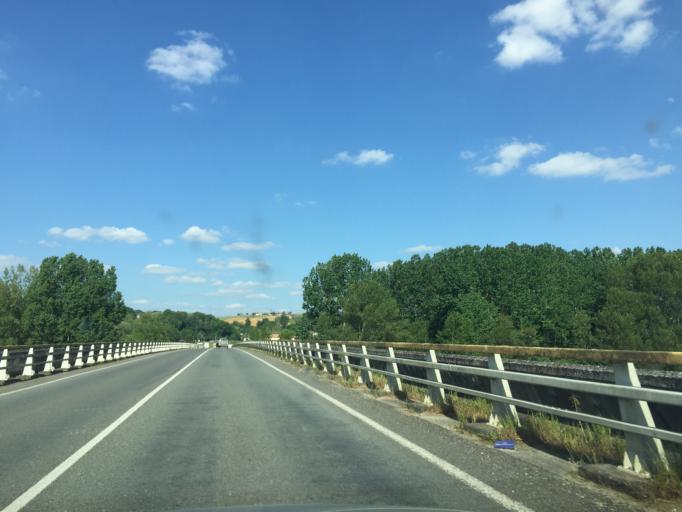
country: FR
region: Aquitaine
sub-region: Departement de la Gironde
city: La Reole
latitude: 44.5718
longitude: -0.0209
